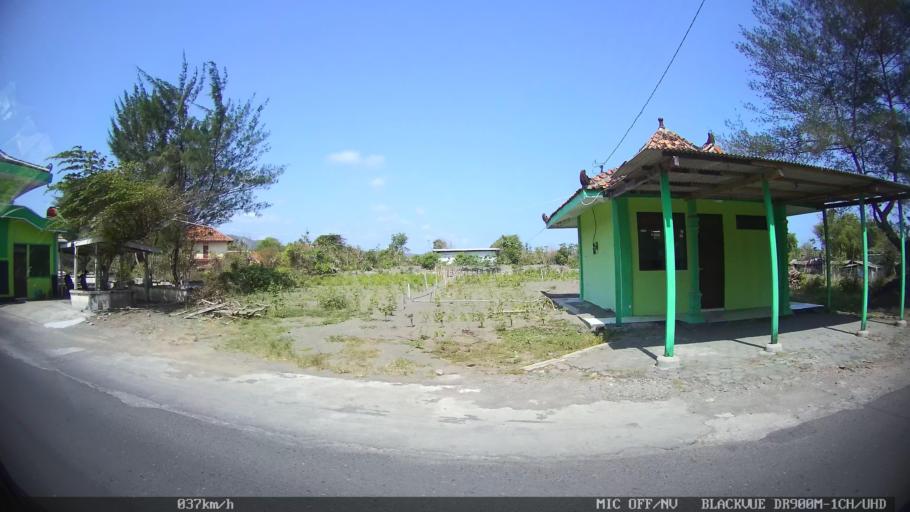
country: ID
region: Daerah Istimewa Yogyakarta
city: Bambanglipuro
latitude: -8.0101
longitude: 110.2955
